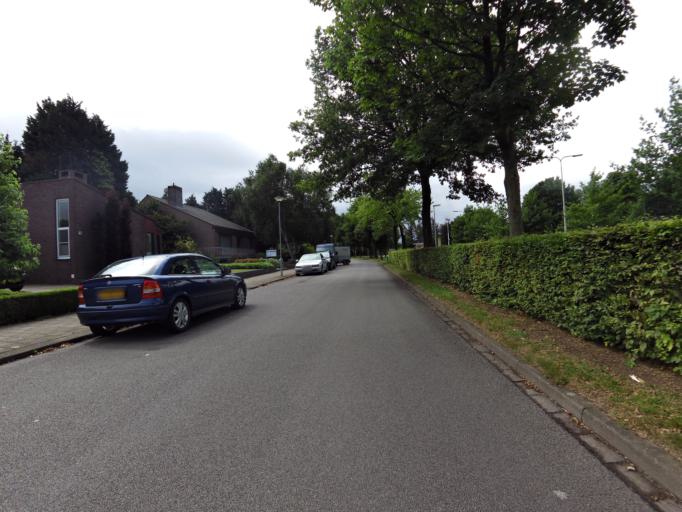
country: NL
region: Limburg
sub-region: Valkenburg aan de Geul
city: Valkenburg
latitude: 50.8845
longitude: 5.8512
